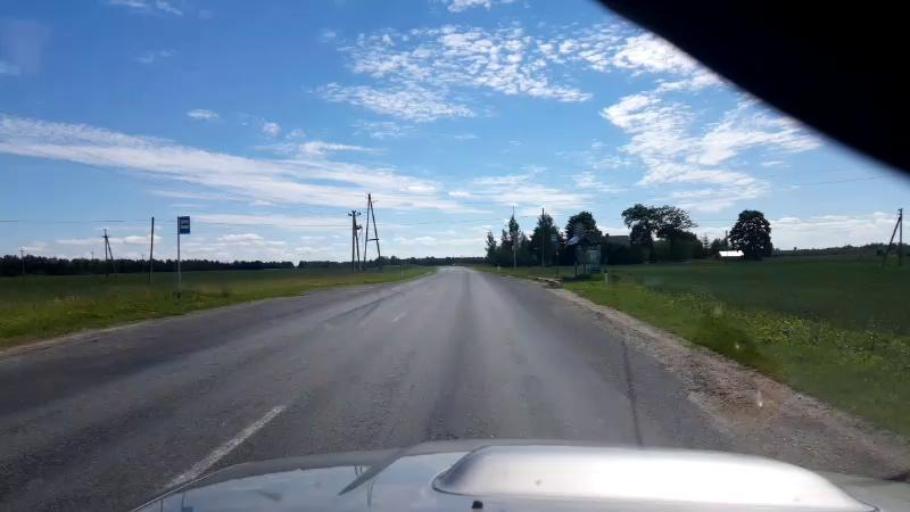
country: EE
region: Laeaene-Virumaa
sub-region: Rakke vald
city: Rakke
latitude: 58.8985
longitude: 26.2828
